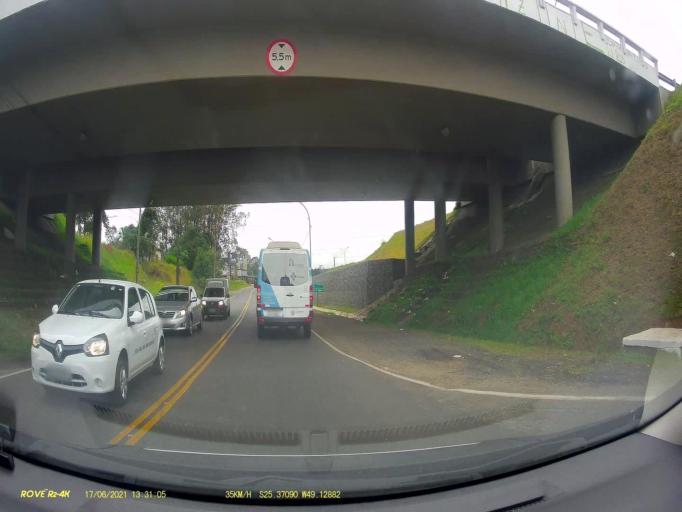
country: BR
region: Parana
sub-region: Quatro Barras
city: Quatro Barras
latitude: -25.3707
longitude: -49.1289
